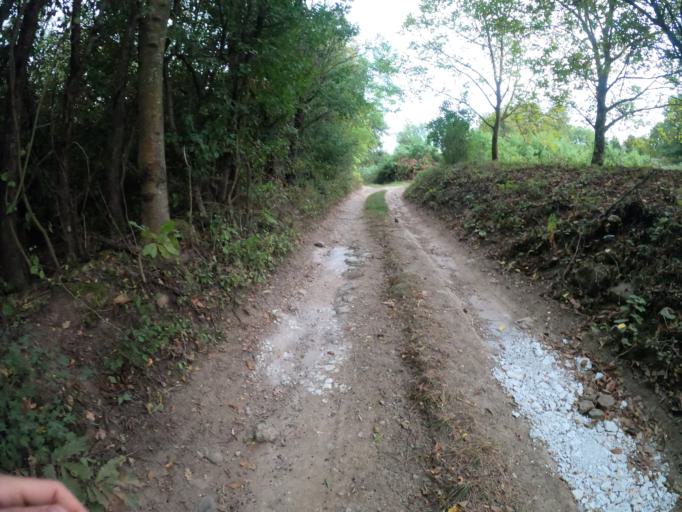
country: HU
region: Veszprem
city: Revfueloep
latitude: 46.8962
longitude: 17.5579
